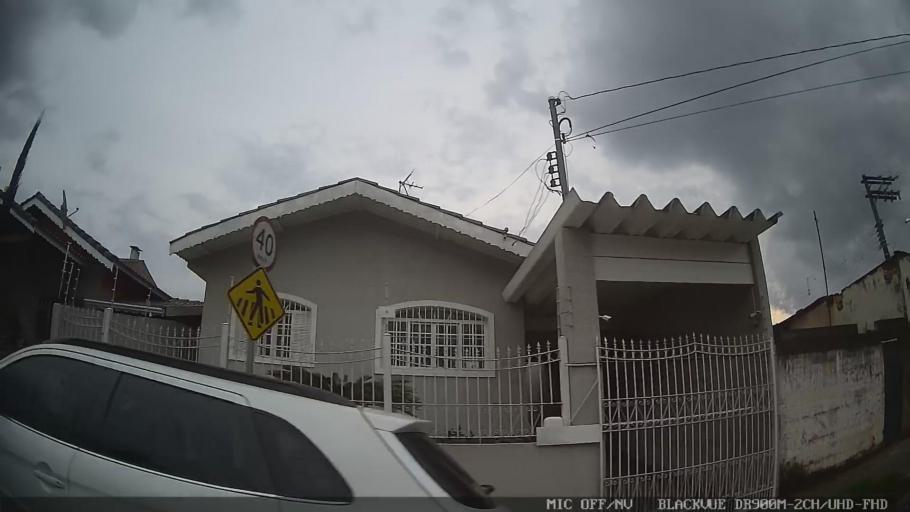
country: BR
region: Sao Paulo
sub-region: Atibaia
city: Atibaia
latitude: -23.1212
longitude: -46.5578
